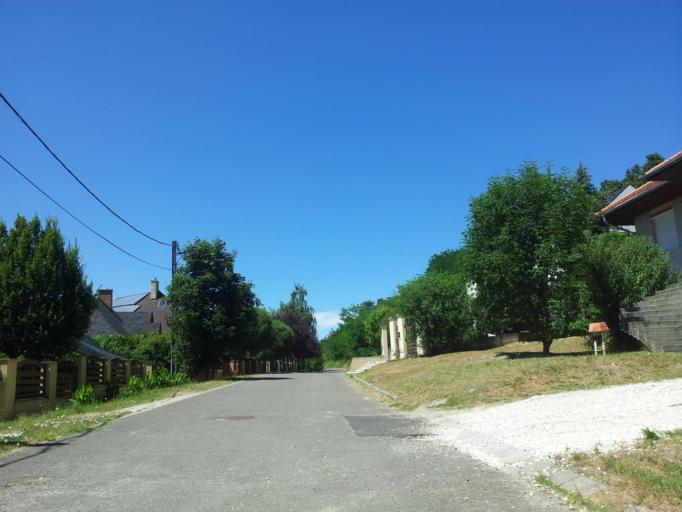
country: HU
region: Pest
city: Erdokertes
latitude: 47.6567
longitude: 19.3128
